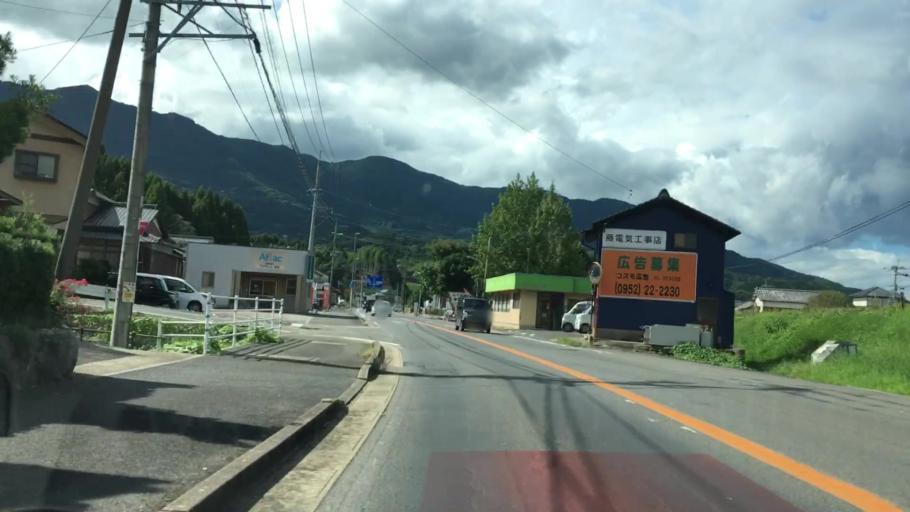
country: JP
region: Saga Prefecture
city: Imaricho-ko
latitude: 33.2219
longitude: 129.8497
